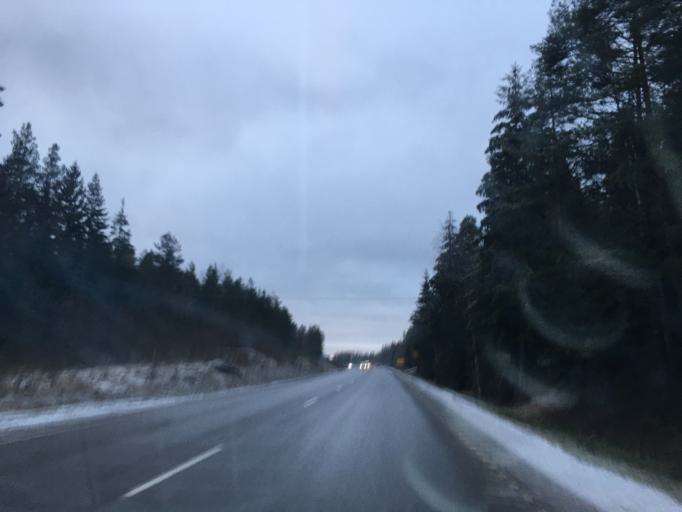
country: FI
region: Varsinais-Suomi
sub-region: Loimaa
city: Aura
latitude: 60.6531
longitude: 22.5539
